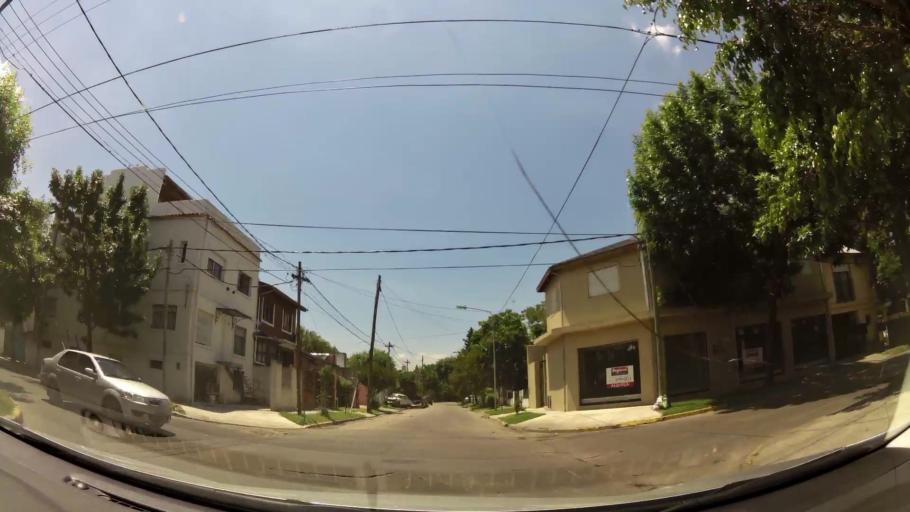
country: AR
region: Buenos Aires
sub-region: Partido de Tigre
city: Tigre
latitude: -34.4217
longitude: -58.5902
